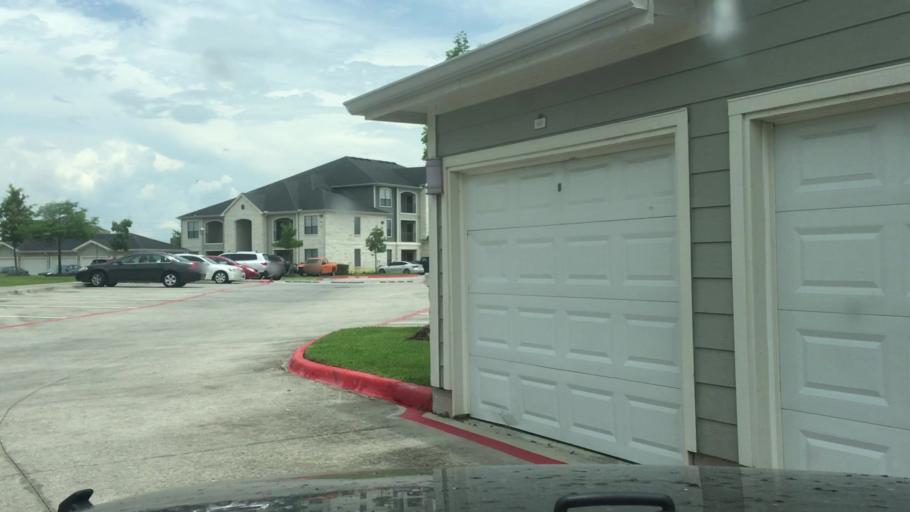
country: US
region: Texas
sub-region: Harris County
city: Humble
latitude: 29.9332
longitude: -95.2440
